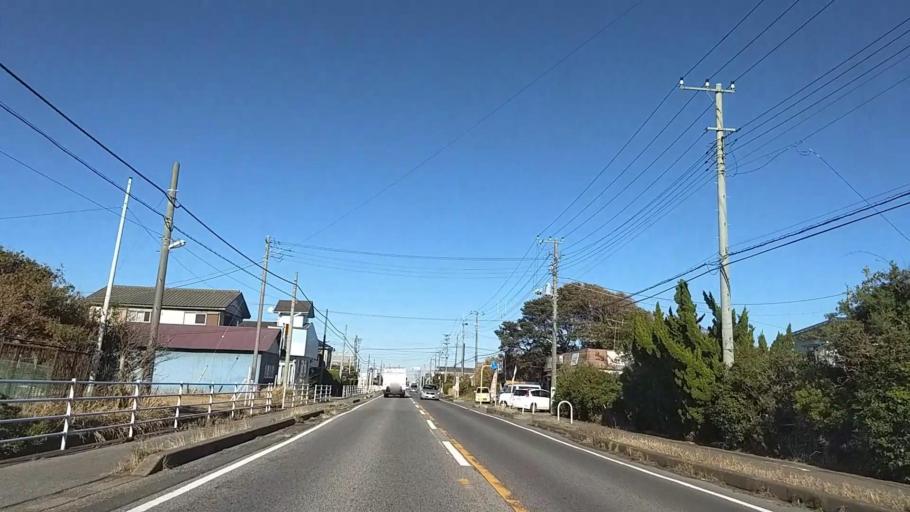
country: JP
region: Chiba
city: Togane
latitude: 35.4902
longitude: 140.4228
